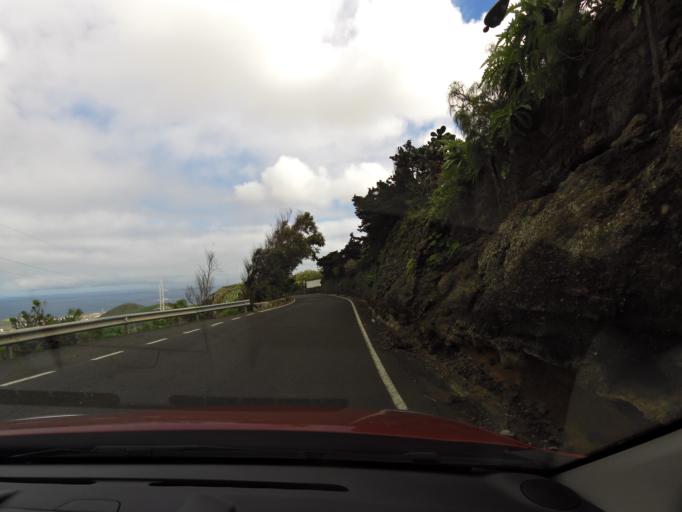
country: ES
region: Canary Islands
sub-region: Provincia de Las Palmas
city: Santa Brigida
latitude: 28.0204
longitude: -15.4582
